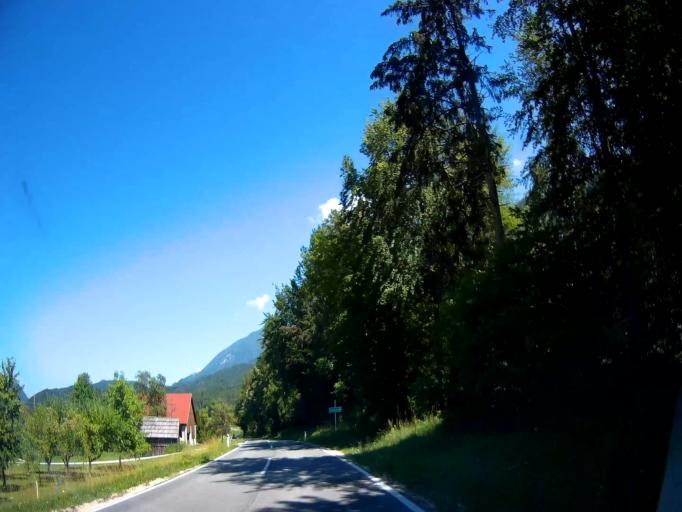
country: AT
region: Carinthia
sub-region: Politischer Bezirk Klagenfurt Land
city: Ebenthal
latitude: 46.5392
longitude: 14.3754
